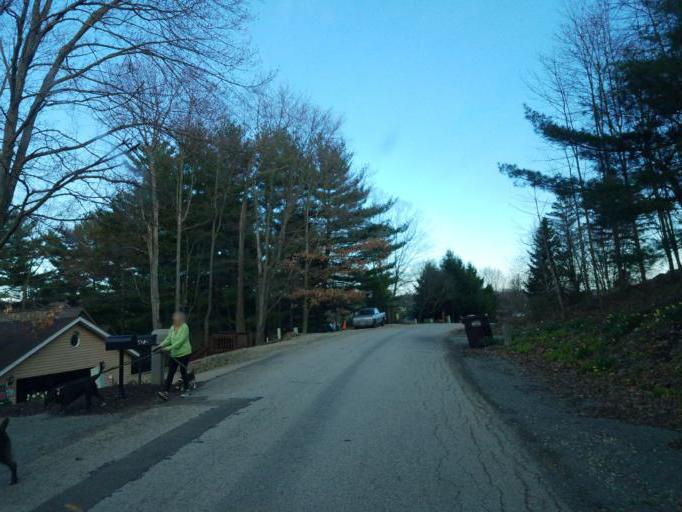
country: US
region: Ohio
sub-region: Knox County
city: Gambier
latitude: 40.4301
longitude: -82.3527
